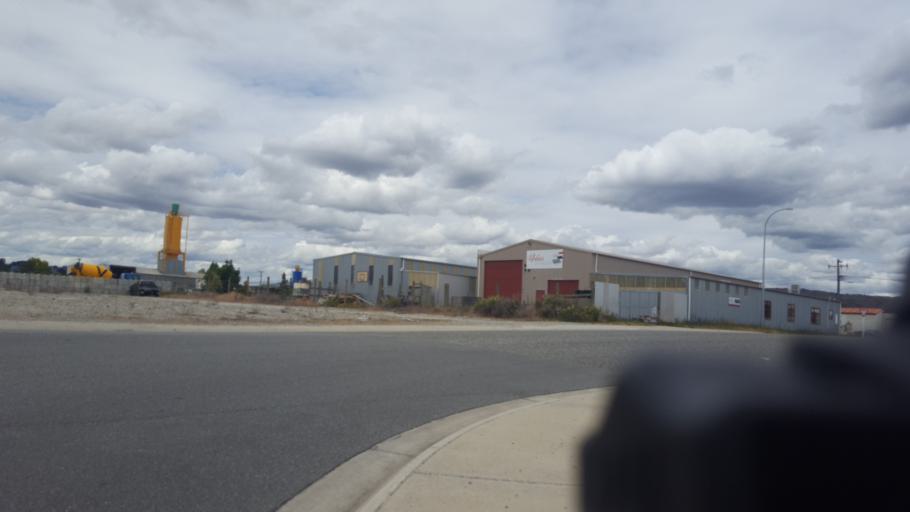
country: NZ
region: Otago
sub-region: Queenstown-Lakes District
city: Wanaka
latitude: -45.2472
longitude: 169.3721
